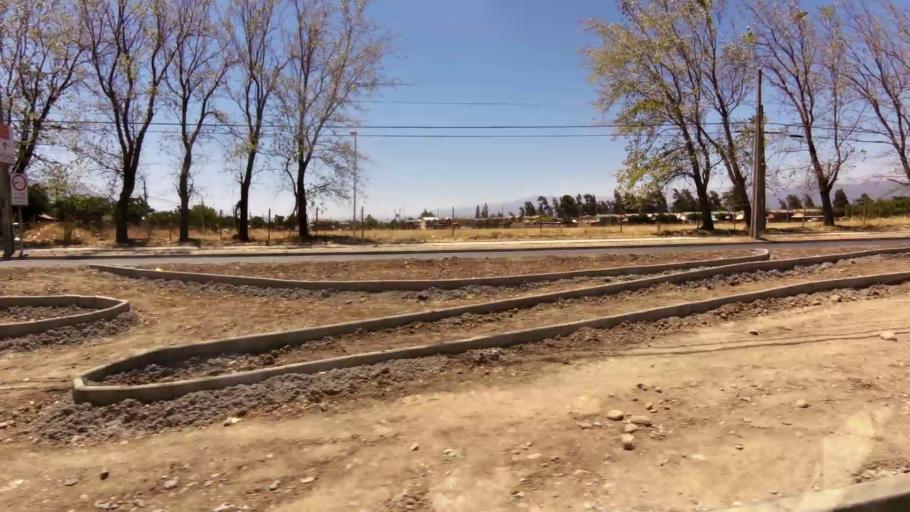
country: CL
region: O'Higgins
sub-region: Provincia de Cachapoal
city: Rancagua
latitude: -34.1580
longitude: -70.7647
